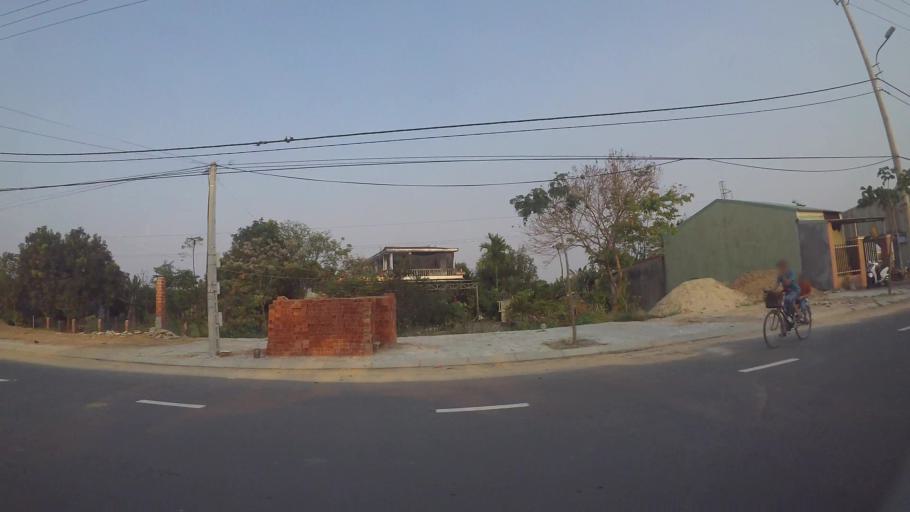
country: VN
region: Da Nang
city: Ngu Hanh Son
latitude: 15.9669
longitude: 108.2314
